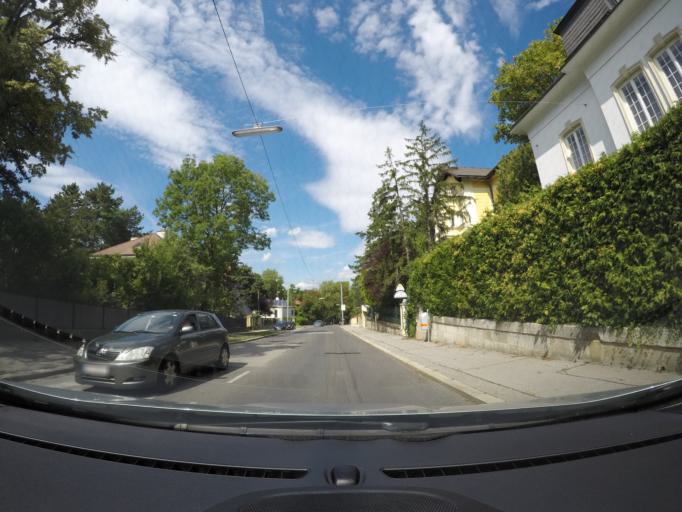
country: AT
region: Lower Austria
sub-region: Politischer Bezirk Modling
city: Perchtoldsdorf
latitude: 48.1833
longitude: 16.2644
